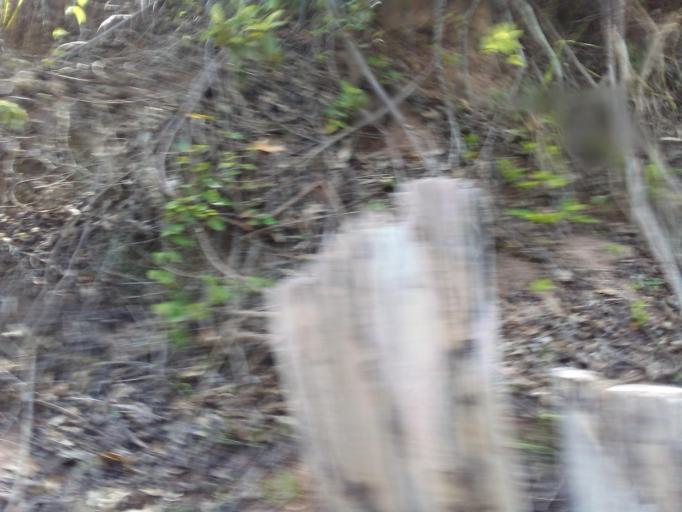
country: BR
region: Espirito Santo
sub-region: Ibiracu
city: Ibiracu
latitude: -19.8474
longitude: -40.3523
